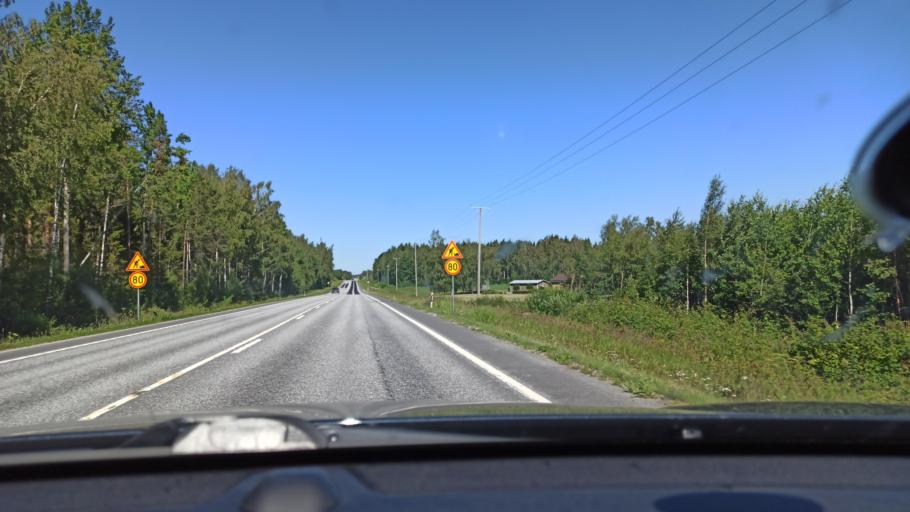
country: FI
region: Ostrobothnia
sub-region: Vaasa
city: Voera
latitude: 63.2307
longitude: 22.2435
